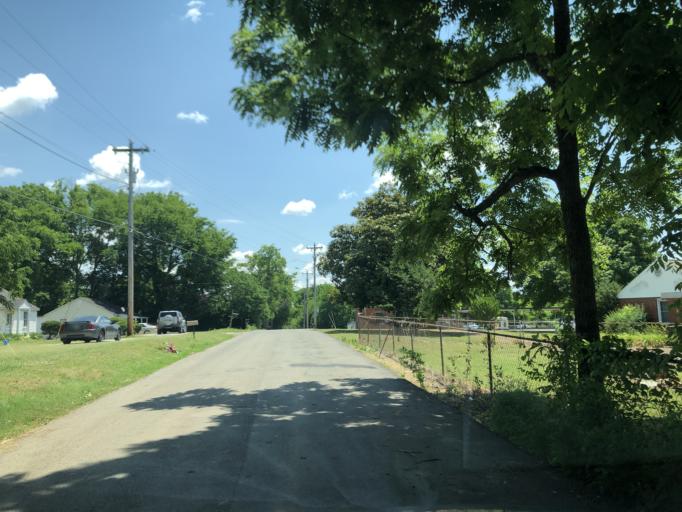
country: US
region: Tennessee
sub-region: Davidson County
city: Goodlettsville
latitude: 36.2682
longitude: -86.7212
